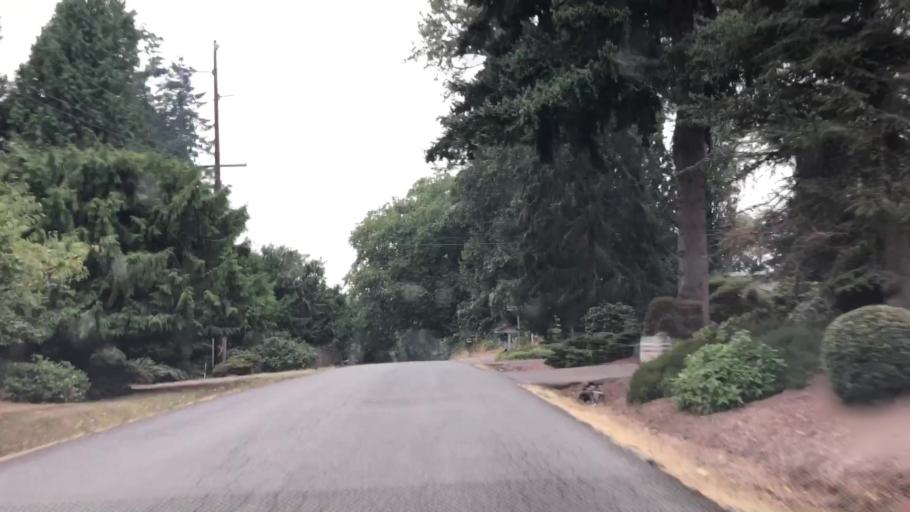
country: US
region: Washington
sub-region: King County
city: Cottage Lake
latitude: 47.7328
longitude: -122.1172
